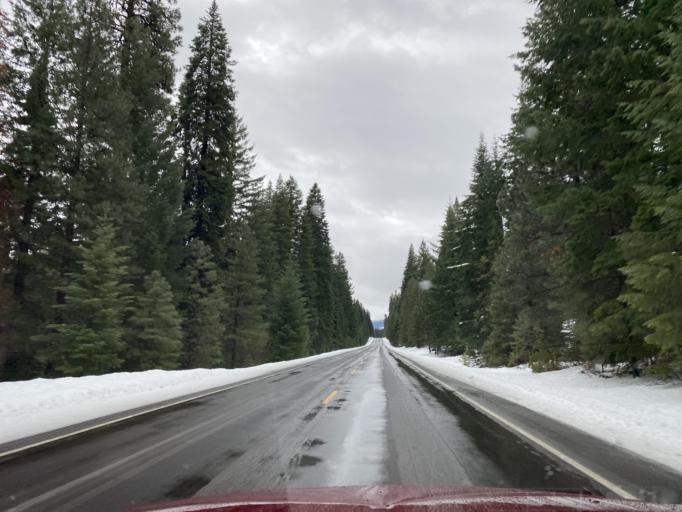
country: US
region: Oregon
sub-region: Klamath County
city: Klamath Falls
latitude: 42.5190
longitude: -122.0840
